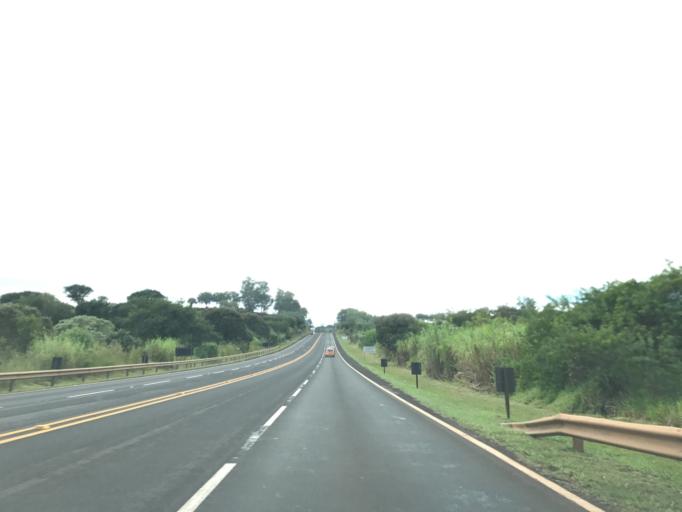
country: BR
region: Parana
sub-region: Arapongas
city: Arapongas
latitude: -23.4524
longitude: -51.5569
